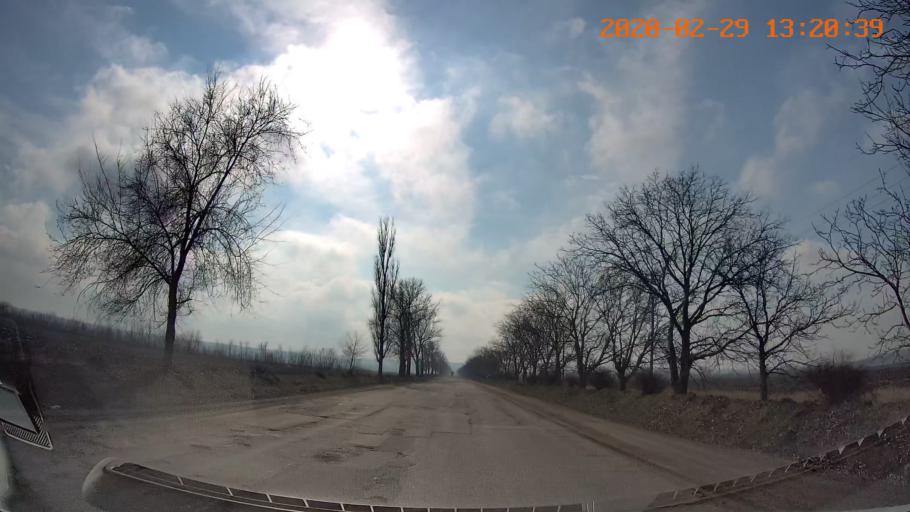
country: MD
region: Telenesti
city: Camenca
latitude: 47.9770
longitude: 28.6396
